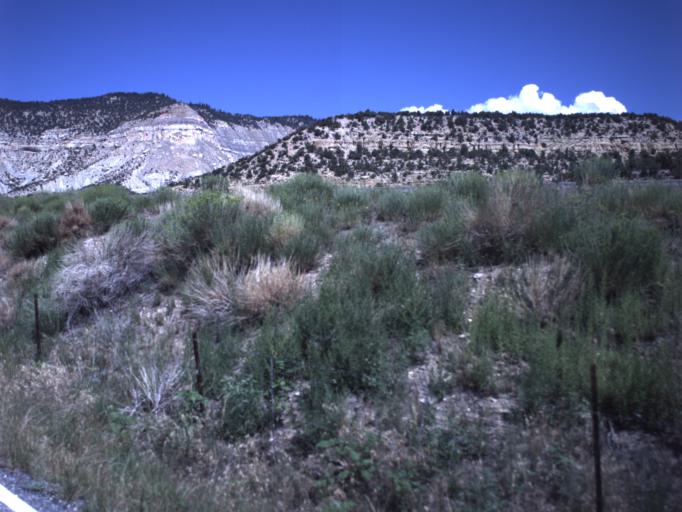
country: US
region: Utah
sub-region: Wayne County
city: Loa
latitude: 38.7557
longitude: -111.3989
